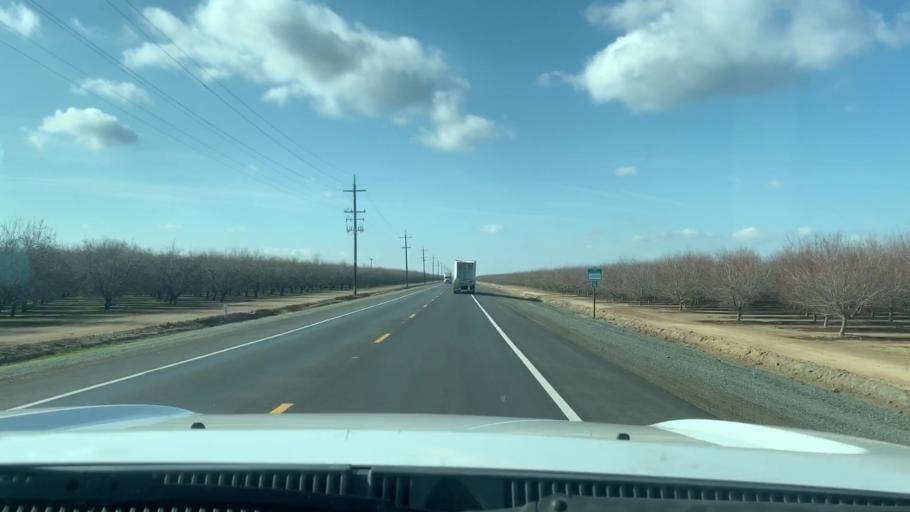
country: US
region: California
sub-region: Kern County
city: McFarland
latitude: 35.6019
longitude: -119.2426
